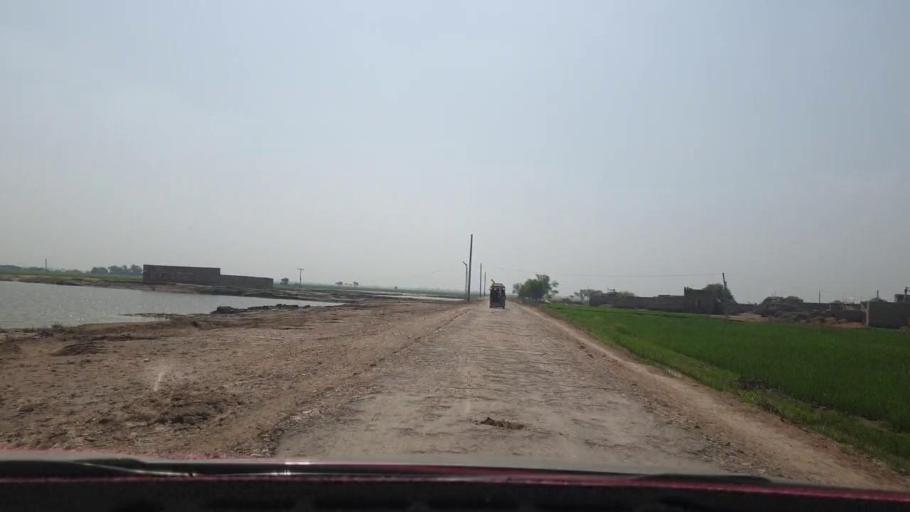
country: PK
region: Sindh
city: Warah
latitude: 27.4051
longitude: 67.8463
